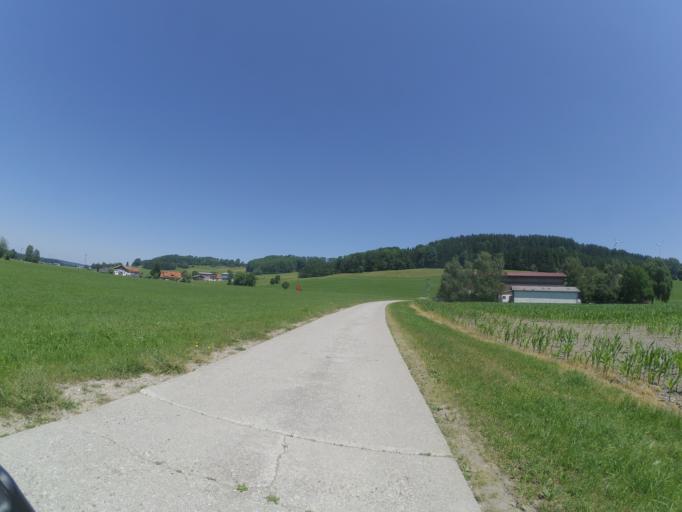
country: DE
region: Bavaria
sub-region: Swabia
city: Bohen
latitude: 47.8724
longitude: 10.3386
